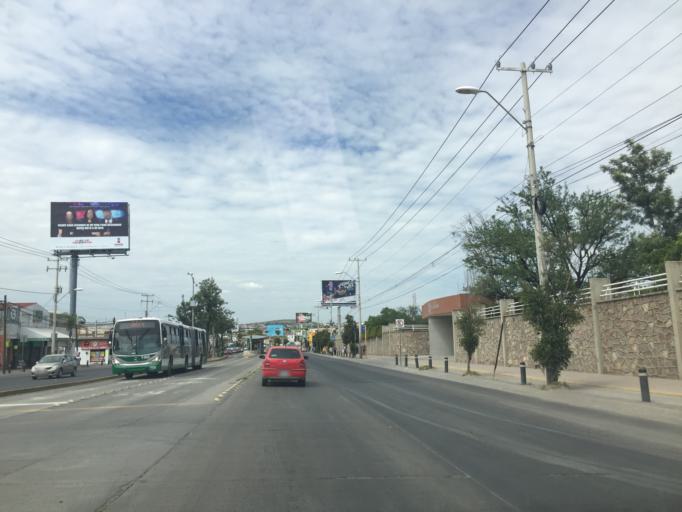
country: MX
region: Guanajuato
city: Leon
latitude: 21.1046
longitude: -101.6948
